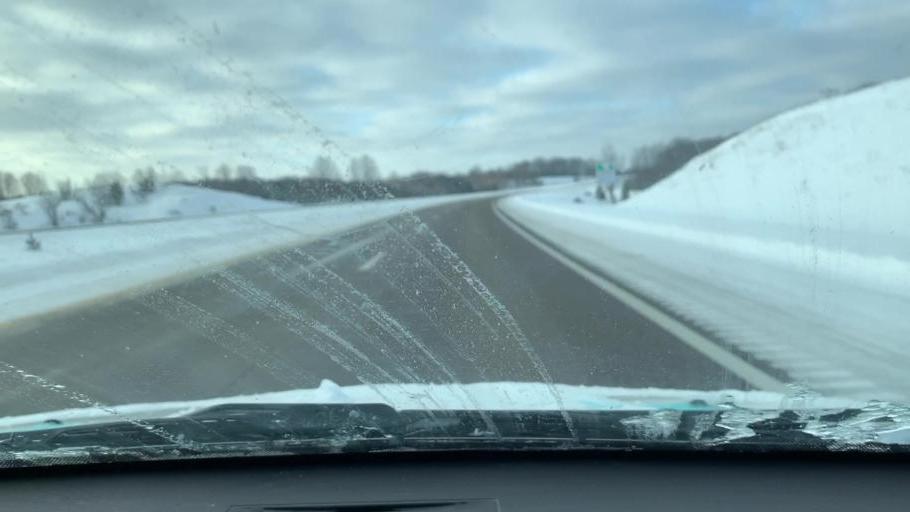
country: US
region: Michigan
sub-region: Wexford County
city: Manton
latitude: 44.3863
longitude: -85.3838
